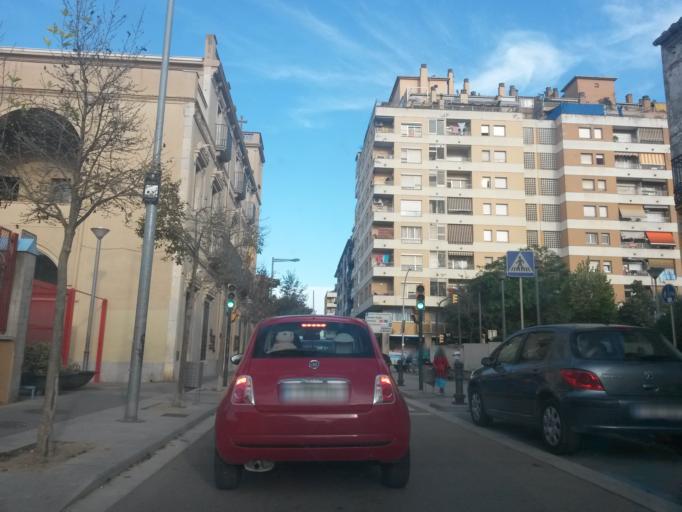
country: ES
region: Catalonia
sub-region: Provincia de Girona
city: Salt
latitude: 41.9751
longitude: 2.7908
